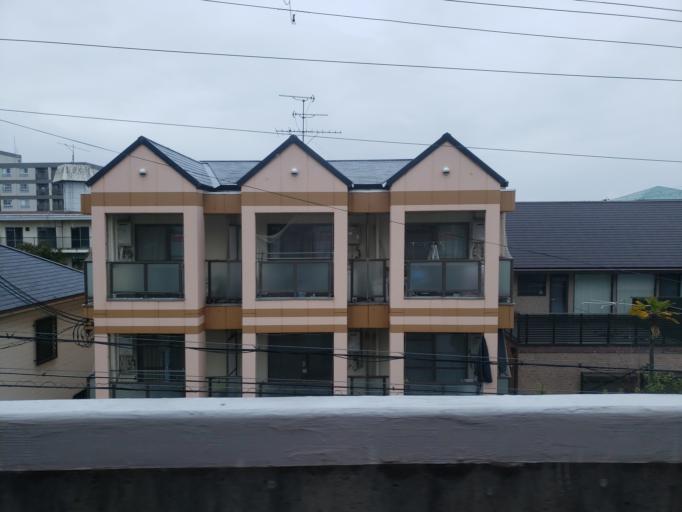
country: JP
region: Hyogo
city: Nishinomiya-hama
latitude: 34.7250
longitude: 135.3611
